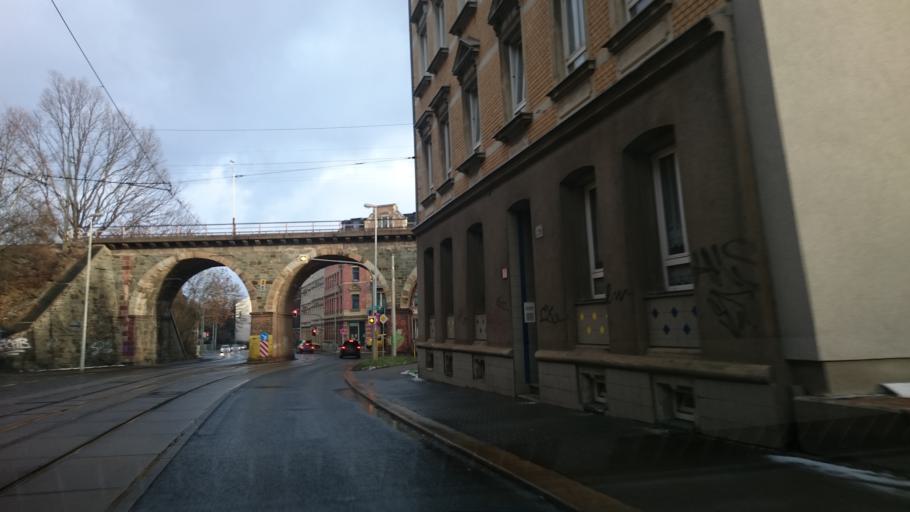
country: DE
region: Saxony
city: Zwickau
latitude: 50.7201
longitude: 12.4793
